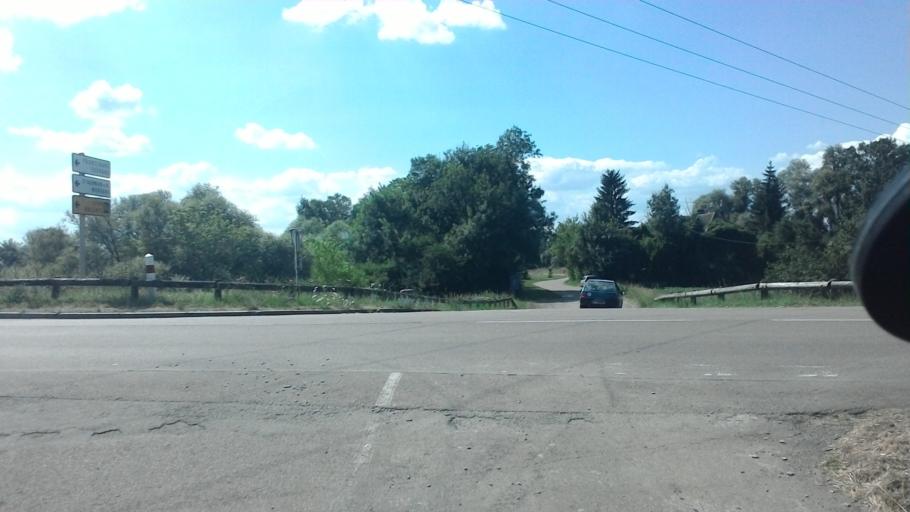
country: FR
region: Bourgogne
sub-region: Departement de la Cote-d'Or
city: Seurre
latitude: 46.9398
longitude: 5.1505
